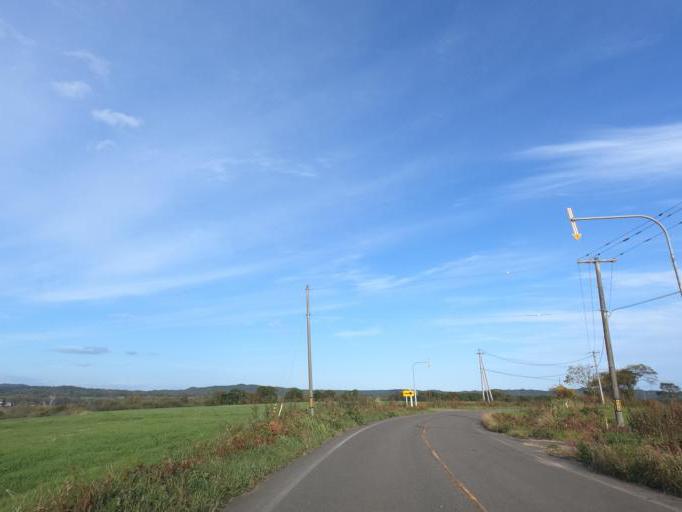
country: JP
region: Hokkaido
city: Obihiro
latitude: 42.5612
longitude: 143.3445
